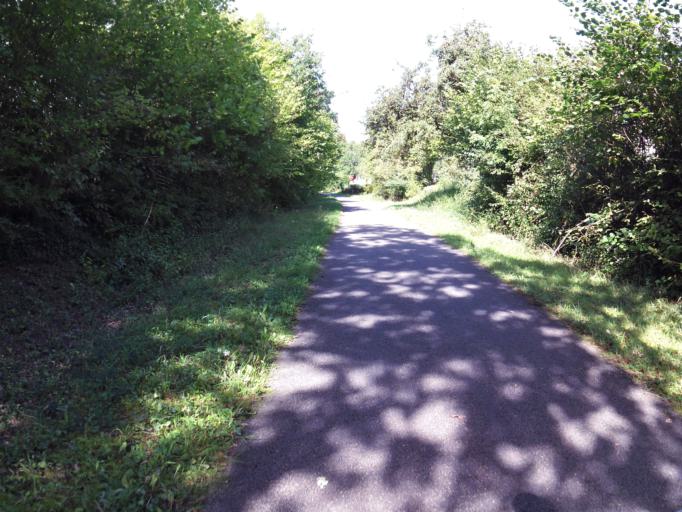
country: DE
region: Rheinland-Pfalz
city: Irrel
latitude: 49.8437
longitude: 6.4713
